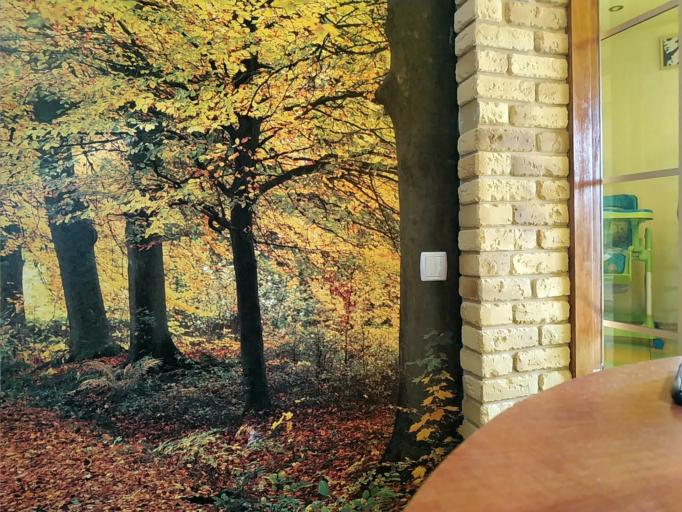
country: RU
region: Novgorod
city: Parfino
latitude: 57.8009
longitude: 31.6106
